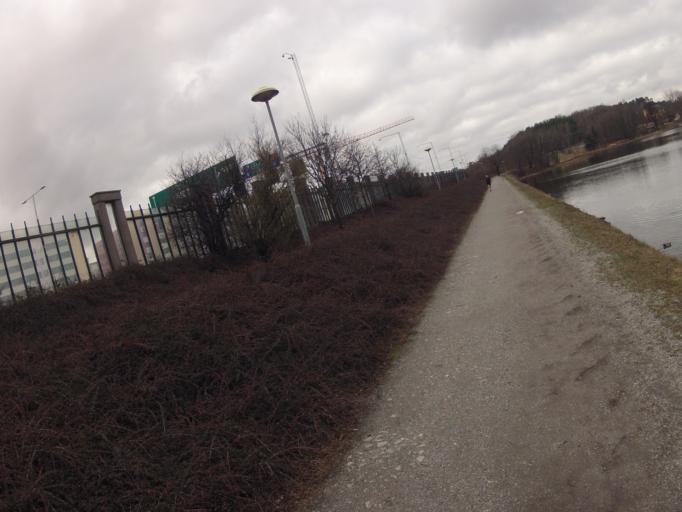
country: SE
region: Stockholm
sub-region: Norrtalje Kommun
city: Bergshamra
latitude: 59.3759
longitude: 18.0162
